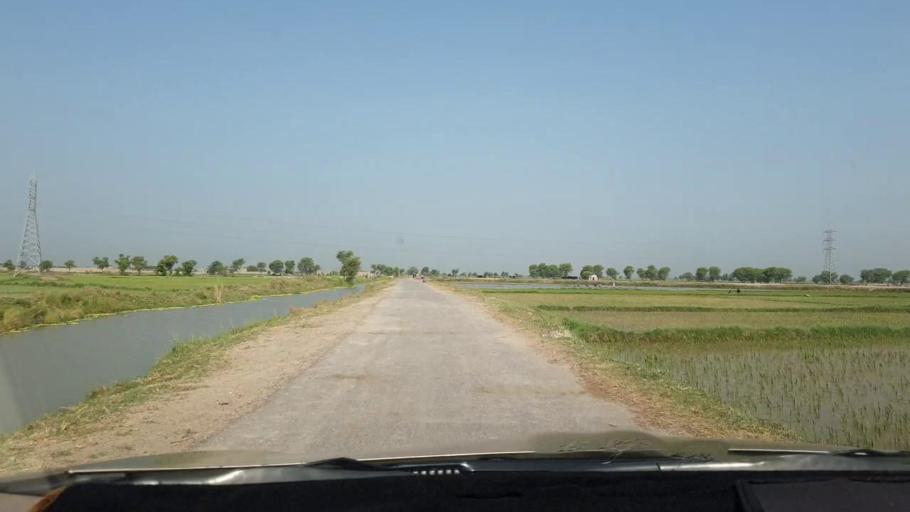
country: PK
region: Sindh
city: Larkana
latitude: 27.6405
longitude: 68.2327
